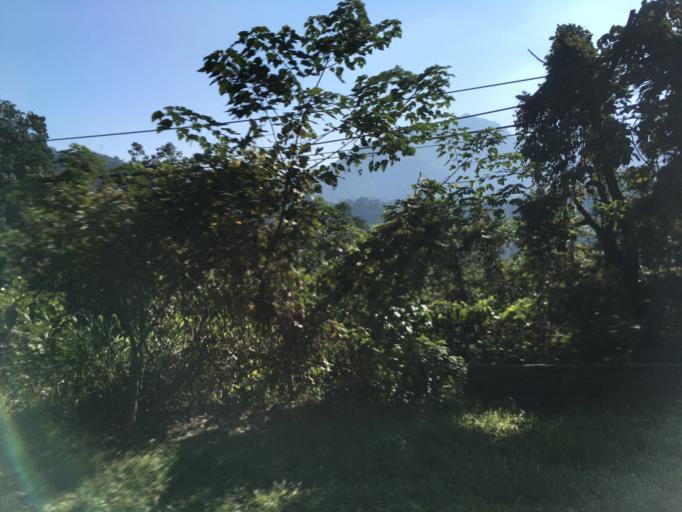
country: TW
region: Taiwan
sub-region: Chiayi
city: Jiayi Shi
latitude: 23.4361
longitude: 120.6283
